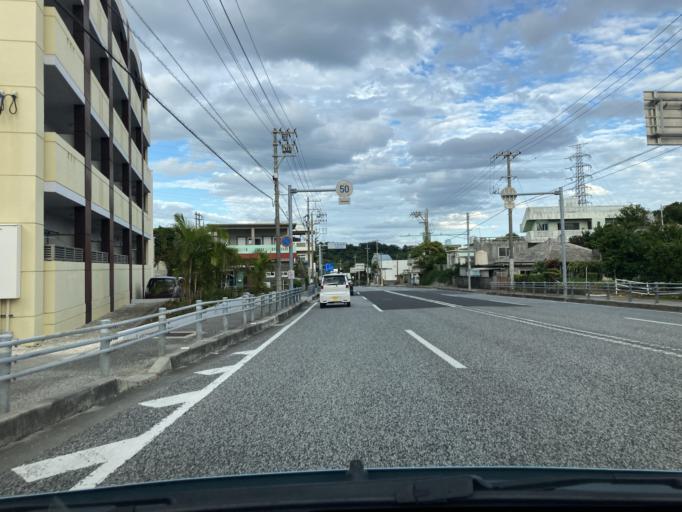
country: JP
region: Okinawa
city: Ishikawa
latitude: 26.3889
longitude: 127.8299
